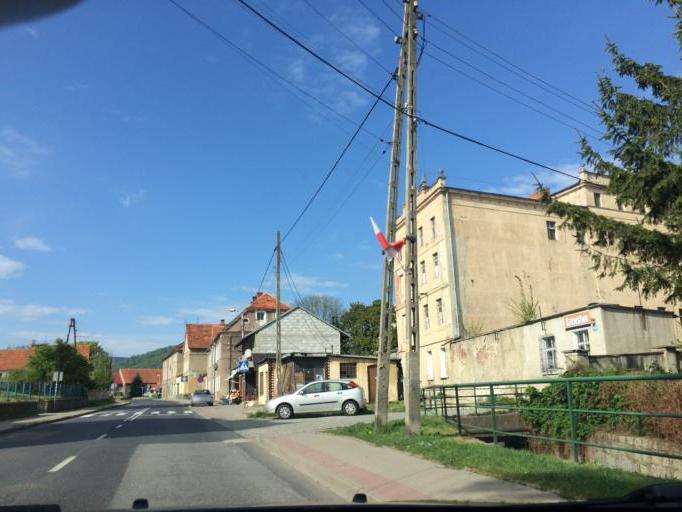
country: PL
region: Lower Silesian Voivodeship
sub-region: Powiat dzierzoniowski
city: Pieszyce
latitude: 50.7132
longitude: 16.5827
